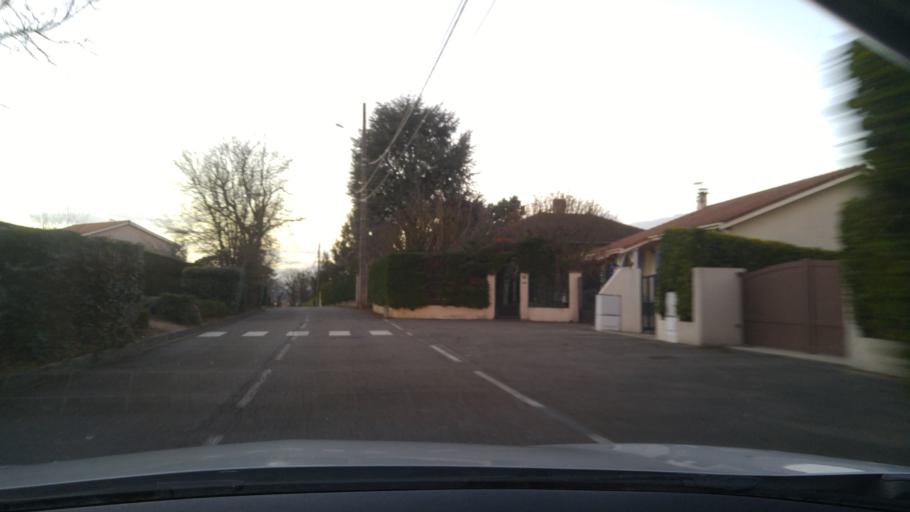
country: FR
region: Rhone-Alpes
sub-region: Departement du Rhone
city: Saint-Bonnet-de-Mure
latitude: 45.6921
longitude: 5.0268
